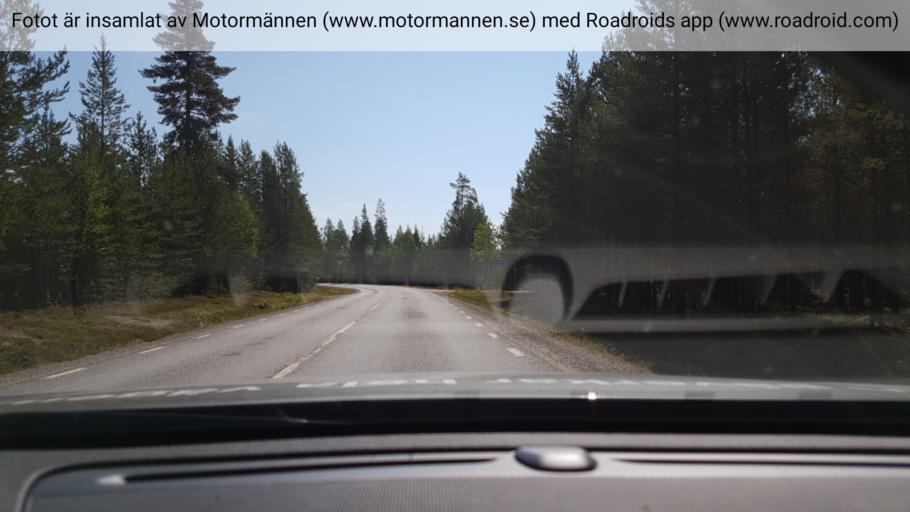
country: SE
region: Vaesterbotten
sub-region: Vindelns Kommun
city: Vindeln
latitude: 64.2495
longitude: 19.6430
